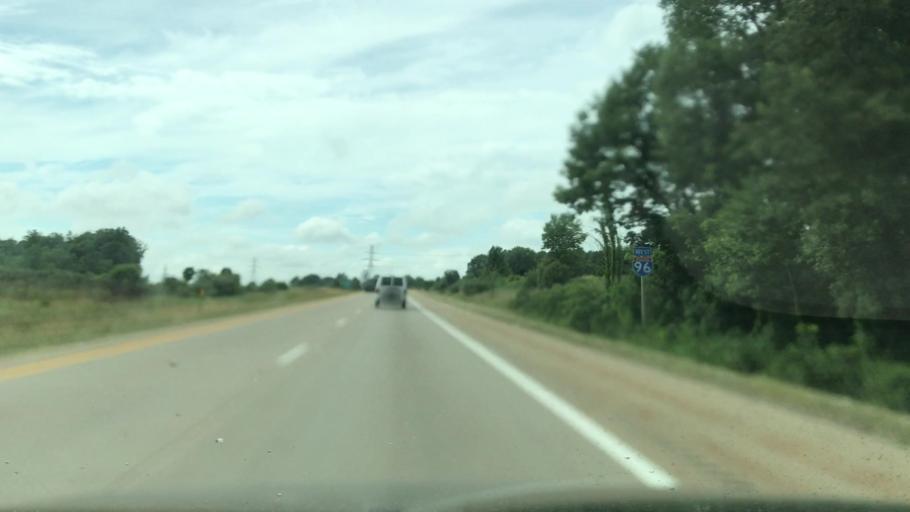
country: US
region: Michigan
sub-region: Kent County
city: Walker
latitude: 43.0228
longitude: -85.7733
